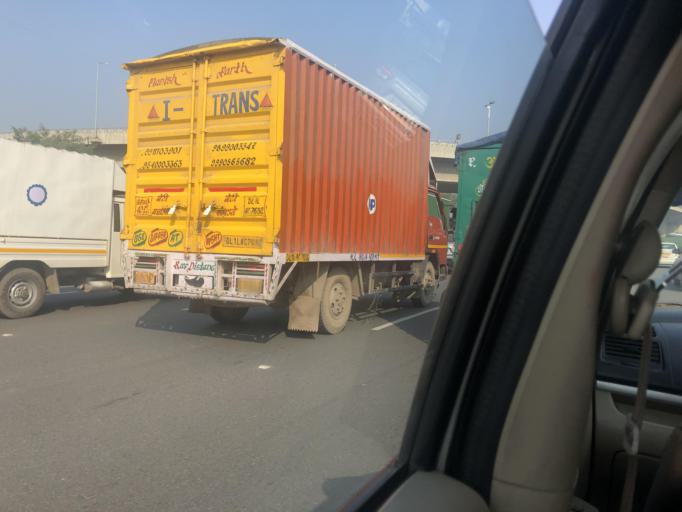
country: IN
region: Haryana
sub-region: Gurgaon
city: Gurgaon
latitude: 28.5393
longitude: 77.1166
